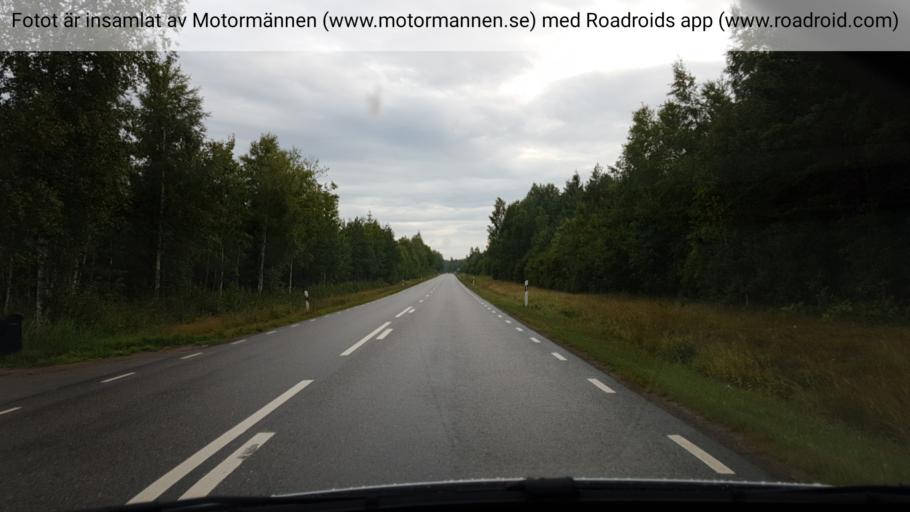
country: SE
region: Vaestra Goetaland
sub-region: Skovde Kommun
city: Stopen
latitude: 58.4463
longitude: 13.9413
